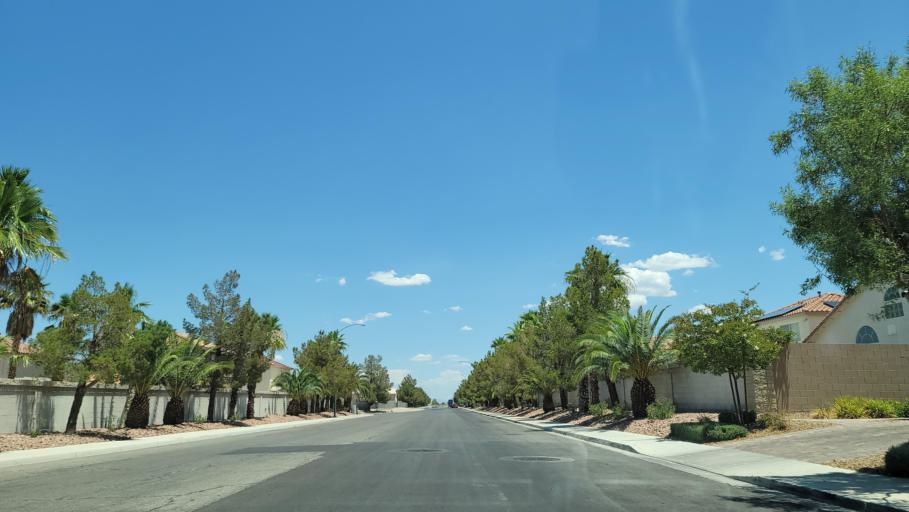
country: US
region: Nevada
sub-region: Clark County
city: Spring Valley
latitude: 36.0814
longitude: -115.2773
